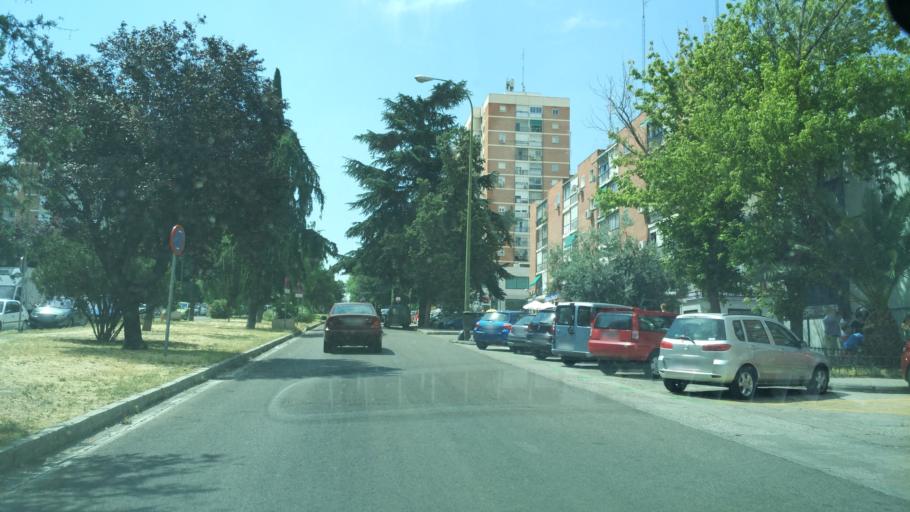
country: ES
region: Madrid
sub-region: Provincia de Madrid
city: Tetuan de las Victorias
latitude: 40.4787
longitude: -3.7041
